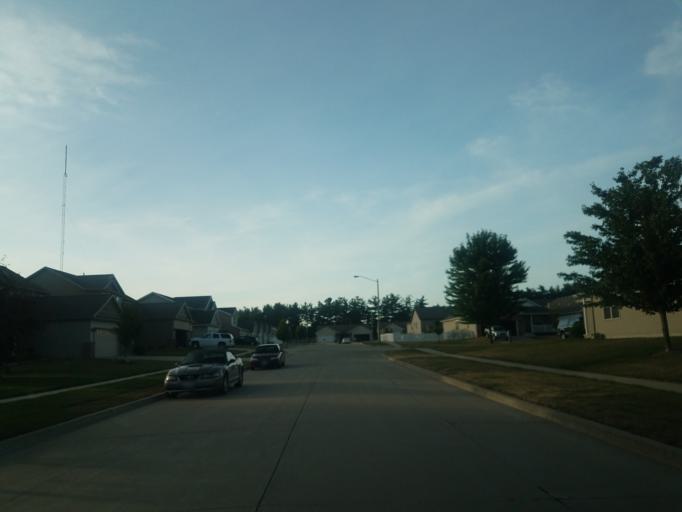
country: US
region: Illinois
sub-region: McLean County
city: Bloomington
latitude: 40.4478
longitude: -89.0099
